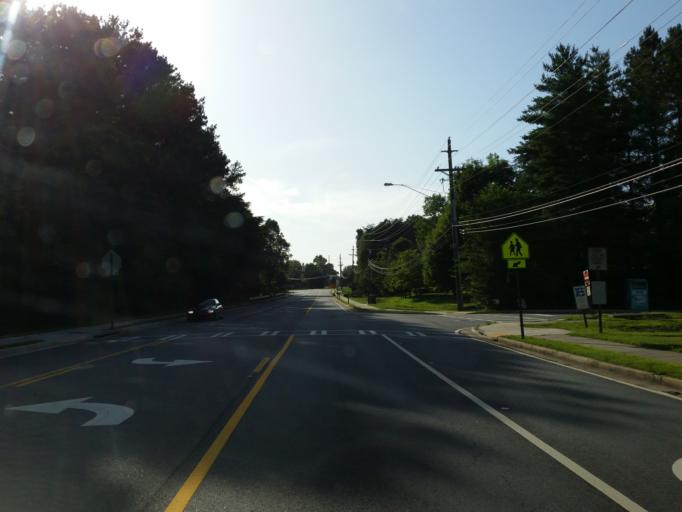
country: US
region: Georgia
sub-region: Cherokee County
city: Woodstock
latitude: 34.0727
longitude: -84.4797
